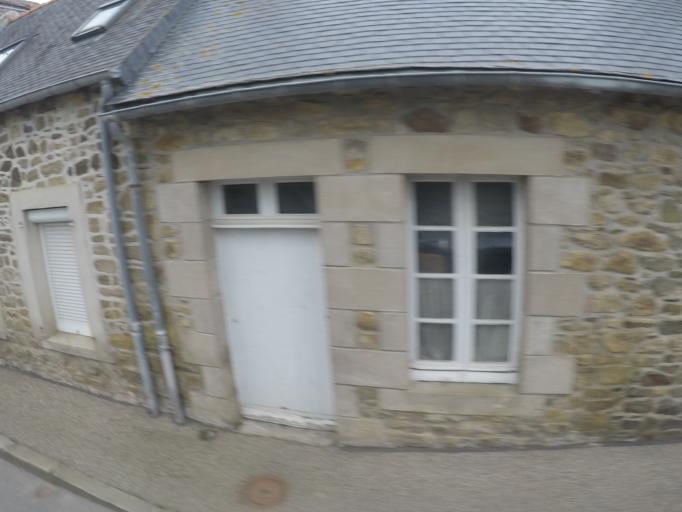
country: FR
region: Brittany
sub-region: Departement des Cotes-d'Armor
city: Pommerit-le-Vicomte
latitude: 48.6401
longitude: -3.0498
